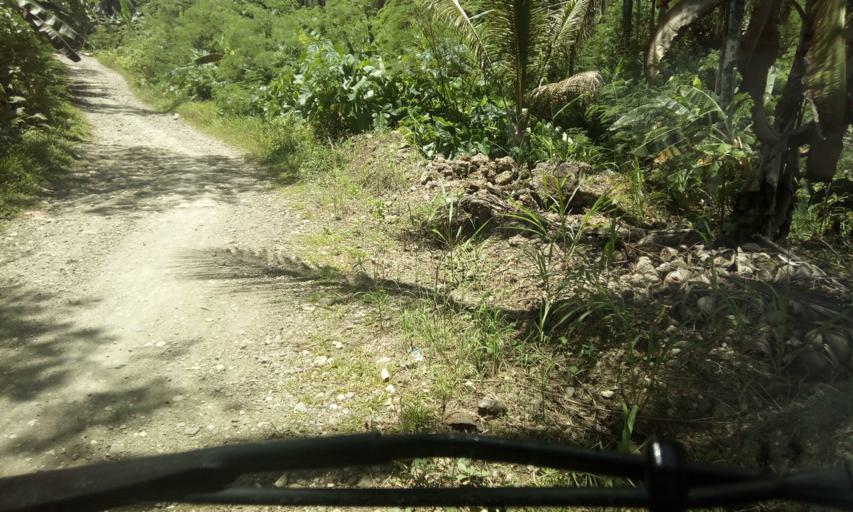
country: PH
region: Caraga
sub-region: Province of Agusan del Sur
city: Santa Josefa
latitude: 7.9553
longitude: 125.9918
